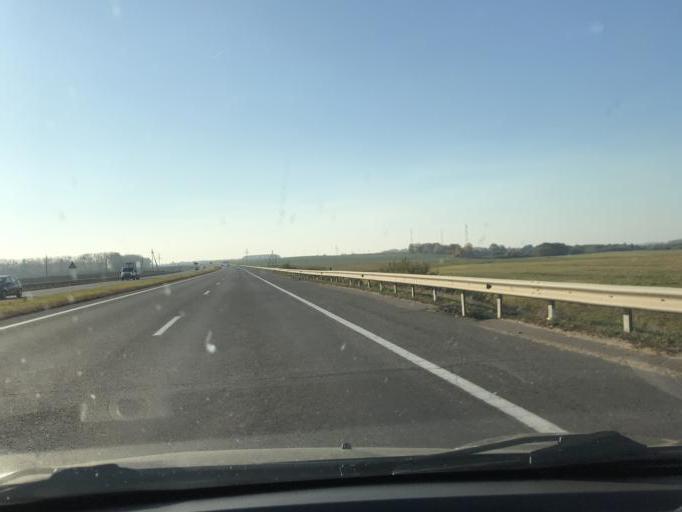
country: BY
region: Minsk
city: Samakhvalavichy
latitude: 53.7334
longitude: 27.5480
